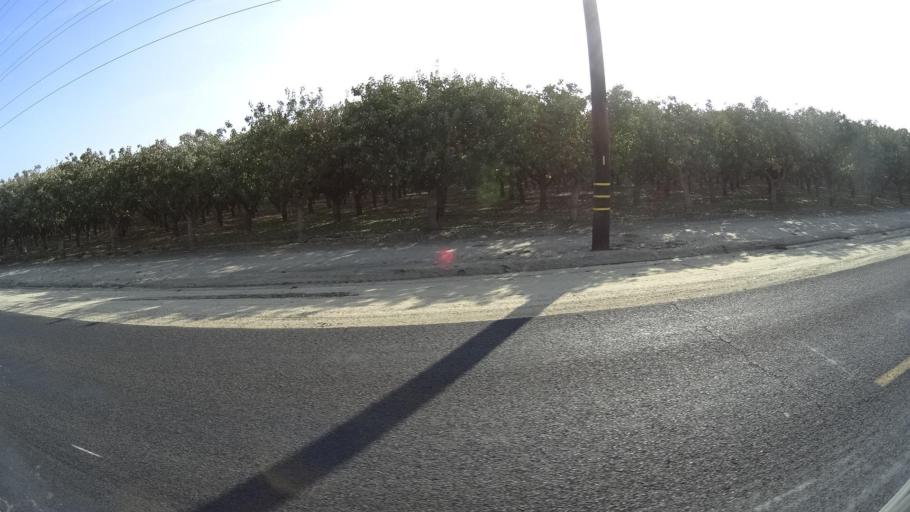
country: US
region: California
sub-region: Kern County
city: Delano
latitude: 35.7759
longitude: -119.2112
